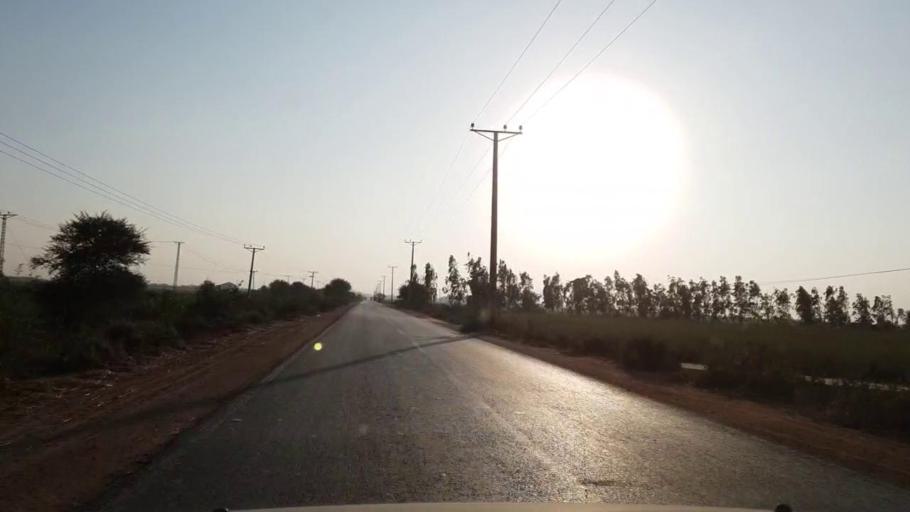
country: PK
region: Sindh
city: Daro Mehar
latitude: 24.6245
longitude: 68.0988
